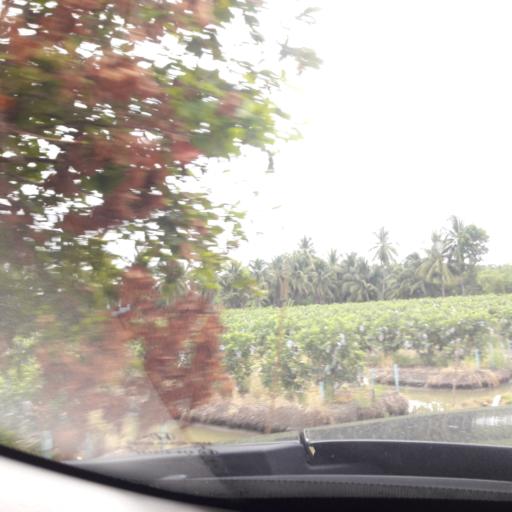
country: TH
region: Ratchaburi
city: Damnoen Saduak
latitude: 13.5703
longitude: 99.9505
